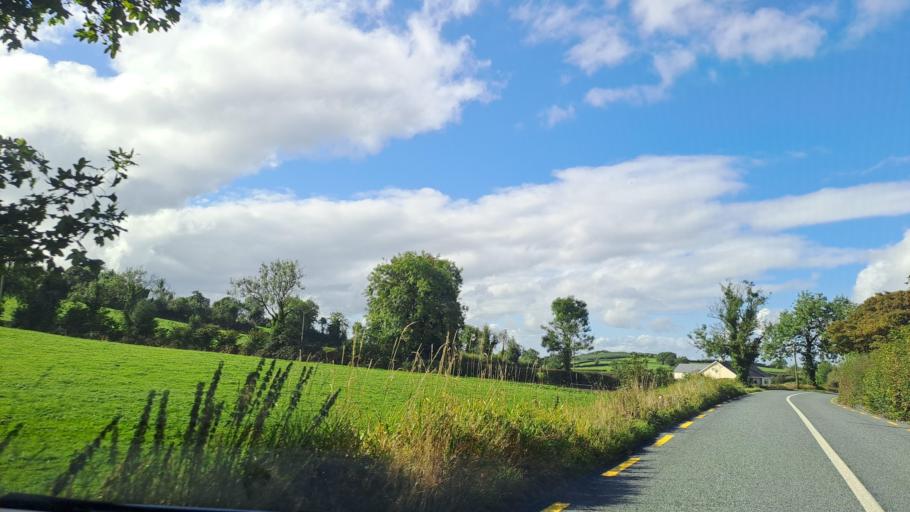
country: IE
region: Ulster
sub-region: An Cabhan
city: Kingscourt
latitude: 53.9755
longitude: -6.8755
